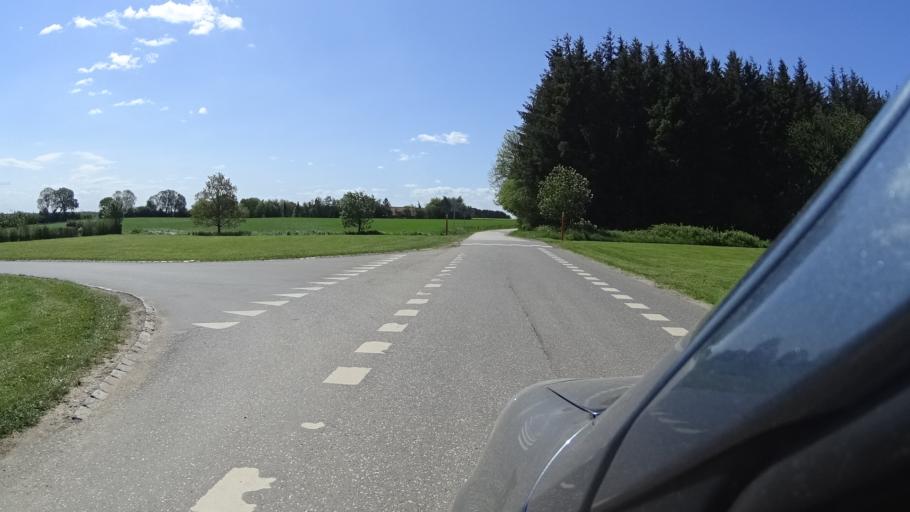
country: DK
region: South Denmark
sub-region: Vejle Kommune
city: Borkop
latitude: 55.6289
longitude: 9.6485
